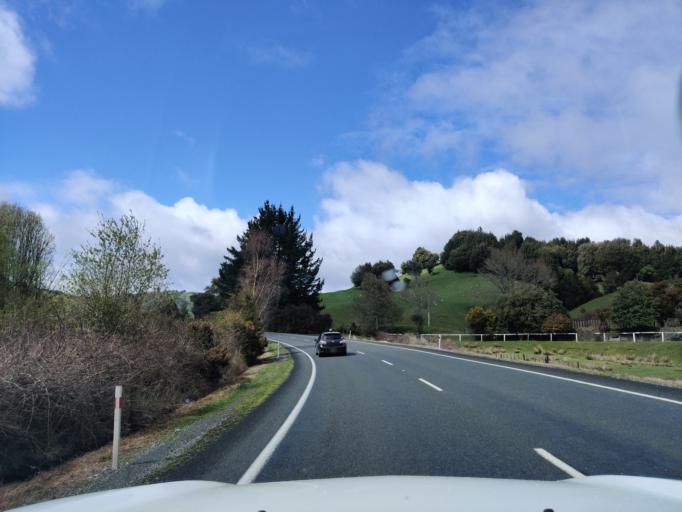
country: NZ
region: Waikato
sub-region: Otorohanga District
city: Otorohanga
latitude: -38.5857
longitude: 175.2153
